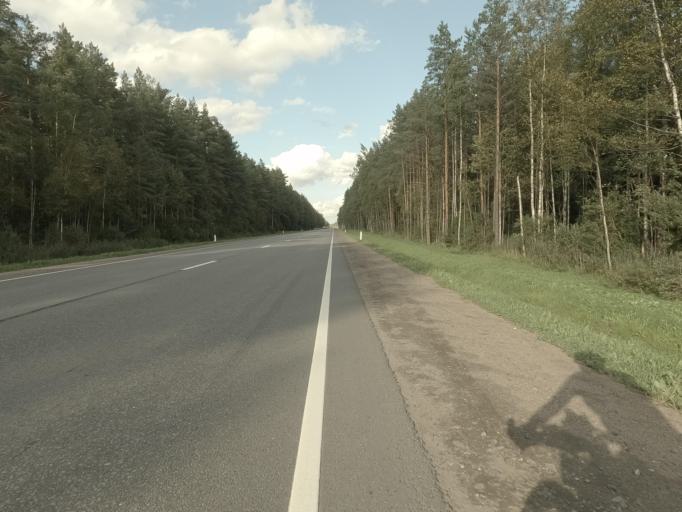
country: RU
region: Leningrad
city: Mga
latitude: 59.7010
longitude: 31.0001
